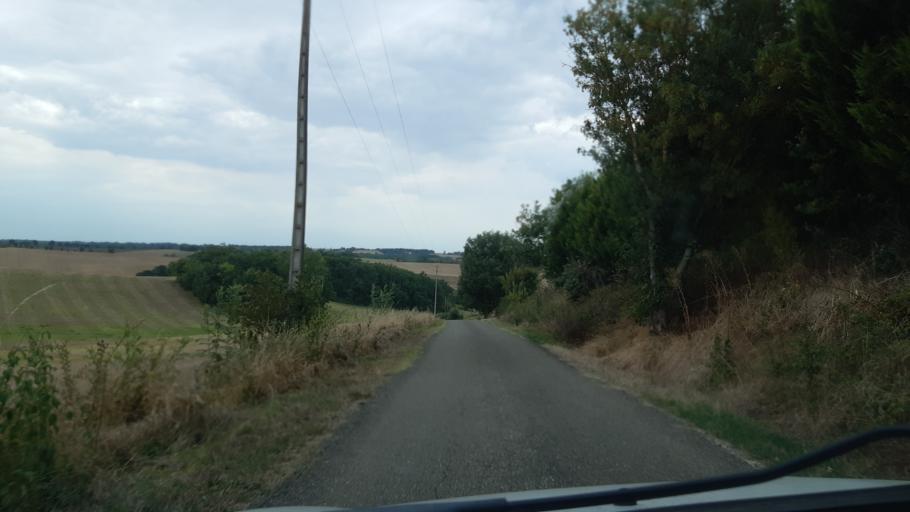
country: FR
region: Midi-Pyrenees
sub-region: Departement du Gers
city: Gimont
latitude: 43.7002
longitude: 0.9871
